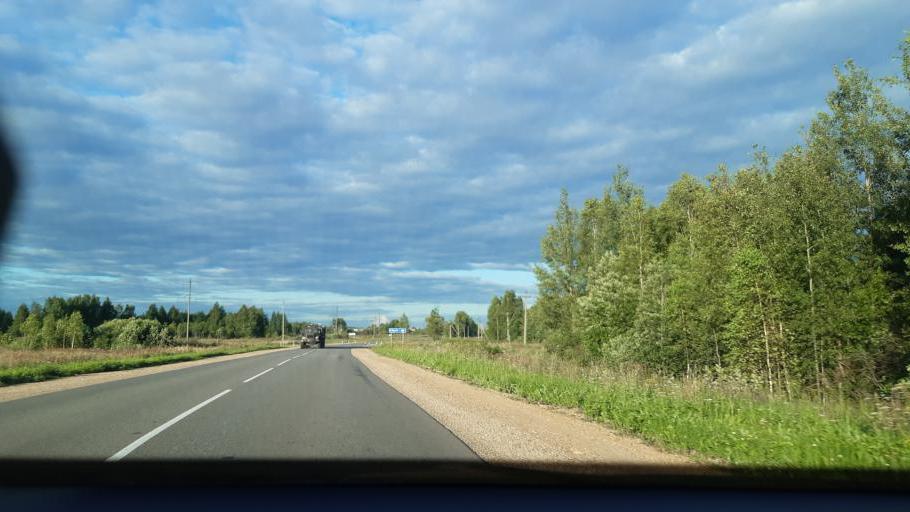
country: RU
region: Smolensk
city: Yel'nya
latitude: 54.5920
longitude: 33.1565
